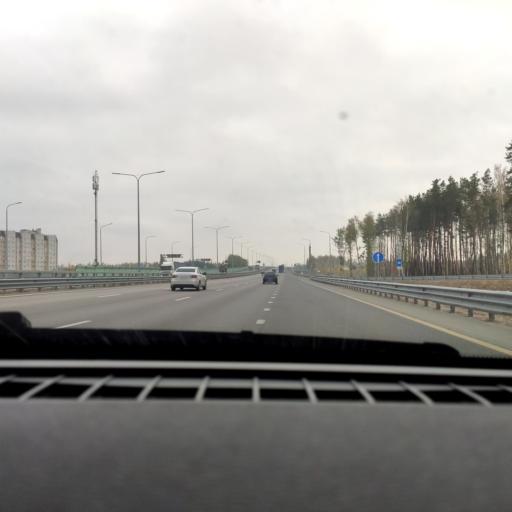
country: RU
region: Voronezj
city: Somovo
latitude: 51.7419
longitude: 39.3072
